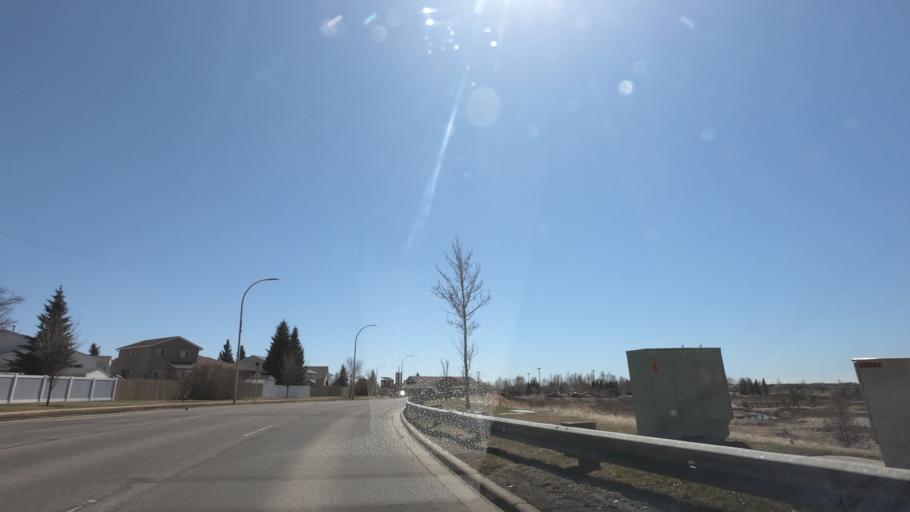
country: CA
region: Alberta
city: Airdrie
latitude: 51.2832
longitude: -114.0113
